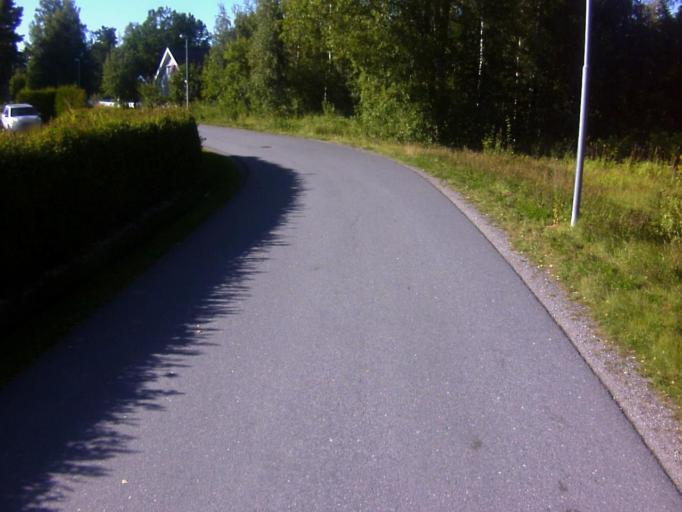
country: SE
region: Soedermanland
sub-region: Eskilstuna Kommun
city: Hallbybrunn
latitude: 59.3393
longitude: 16.4186
